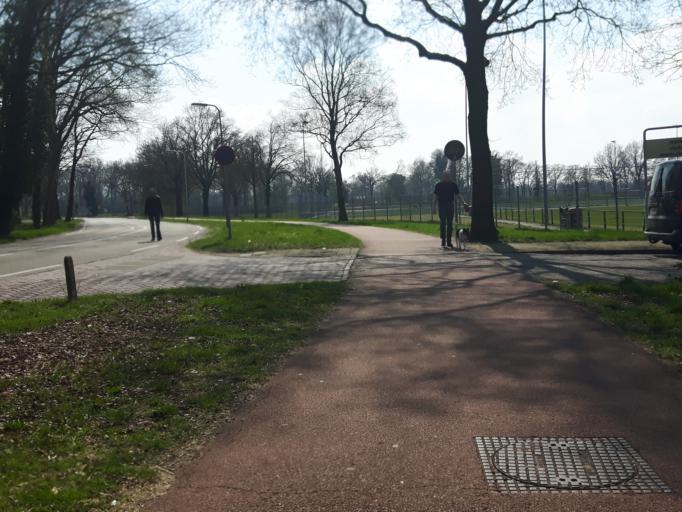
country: NL
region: Overijssel
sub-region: Gemeente Enschede
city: Enschede
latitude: 52.1904
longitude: 6.8650
